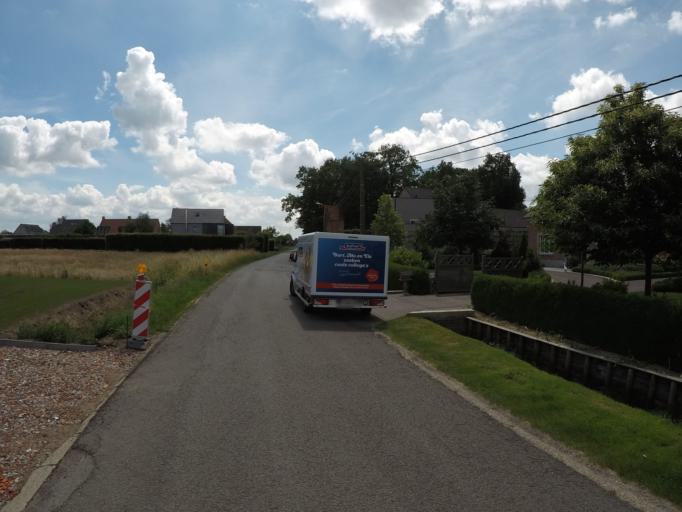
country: BE
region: Flanders
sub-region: Provincie Antwerpen
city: Vosselaar
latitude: 51.2777
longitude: 4.8820
